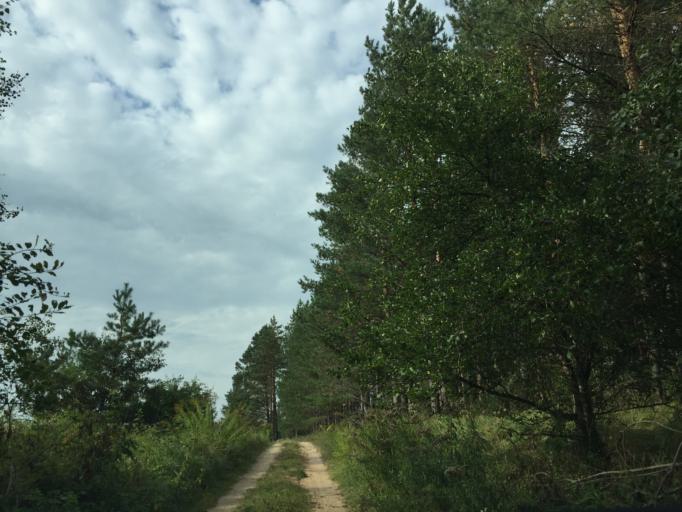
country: LV
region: Baldone
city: Baldone
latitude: 56.7630
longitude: 24.4686
